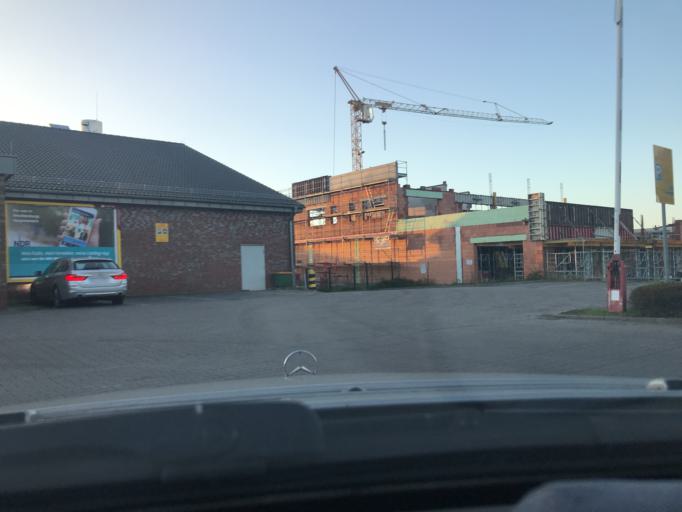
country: DE
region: Mecklenburg-Vorpommern
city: Ostseebad Zinnowitz
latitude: 54.0746
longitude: 13.9090
